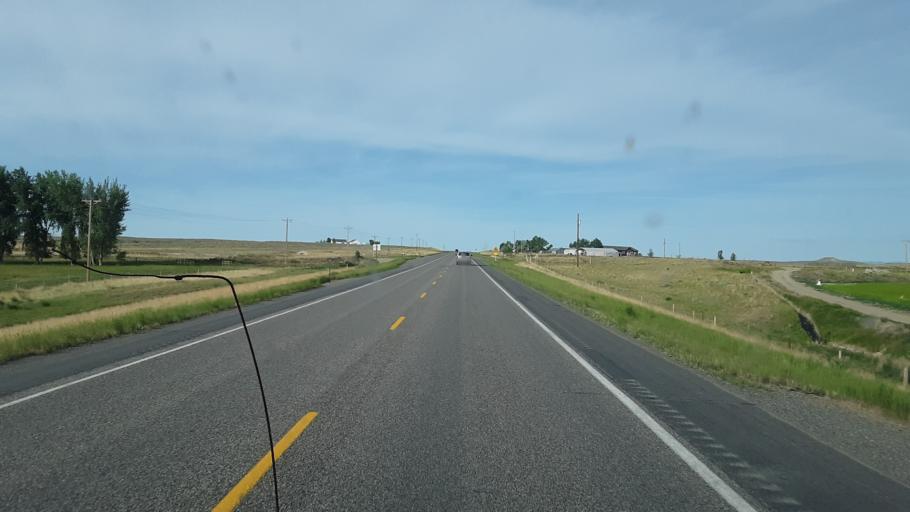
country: US
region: Wyoming
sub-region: Fremont County
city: Riverton
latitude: 43.1679
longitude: -108.2626
